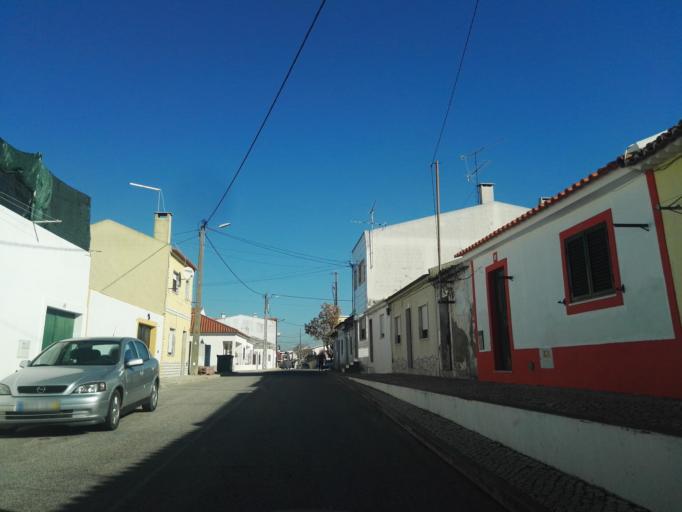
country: PT
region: Santarem
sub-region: Benavente
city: Samora Correia
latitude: 38.9355
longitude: -8.8753
